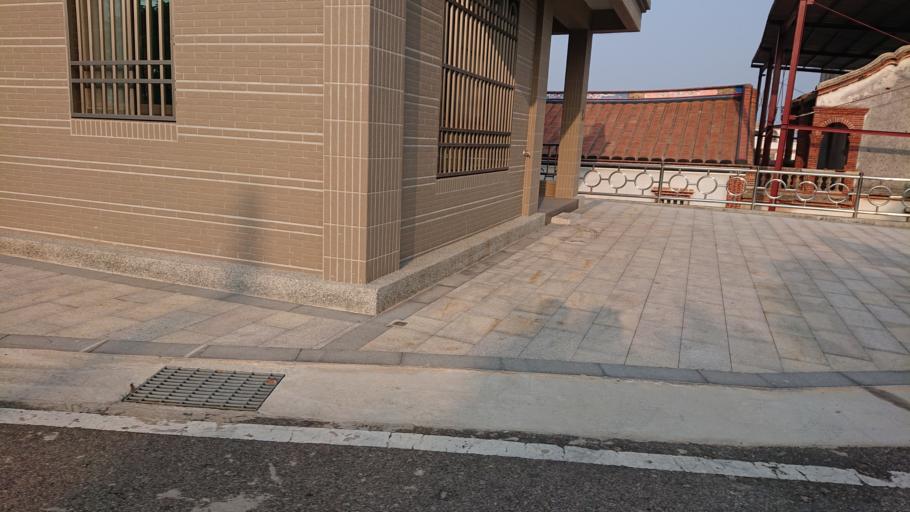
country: TW
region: Fukien
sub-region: Kinmen
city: Jincheng
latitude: 24.4460
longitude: 118.2517
